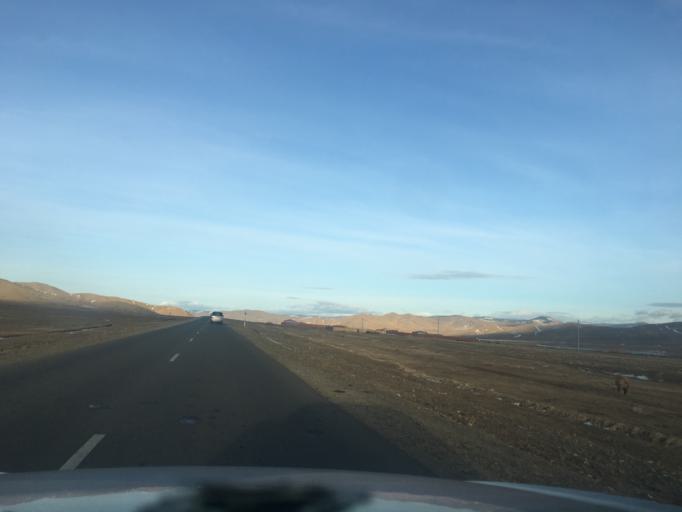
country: MN
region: Central Aimak
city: Mandal
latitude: 48.0975
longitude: 106.6145
